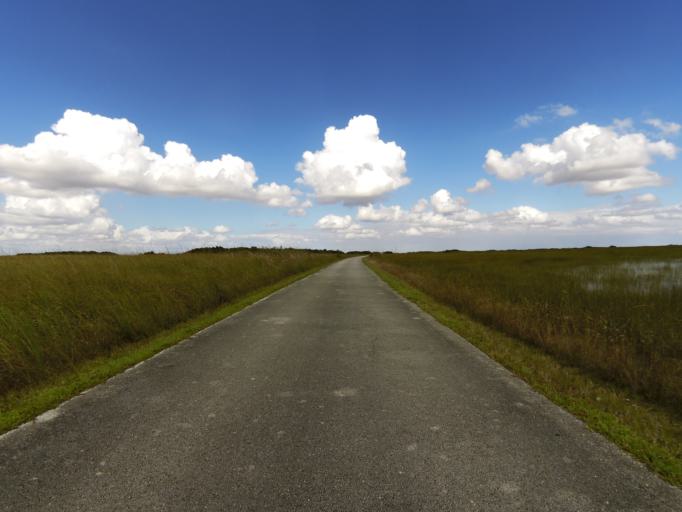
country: US
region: Florida
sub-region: Miami-Dade County
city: The Hammocks
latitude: 25.6683
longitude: -80.7611
